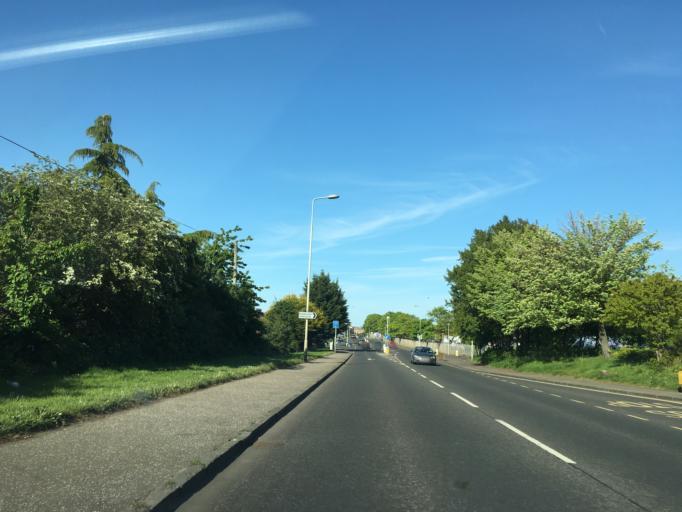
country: GB
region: Scotland
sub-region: Edinburgh
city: Colinton
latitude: 55.9221
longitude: -3.2744
